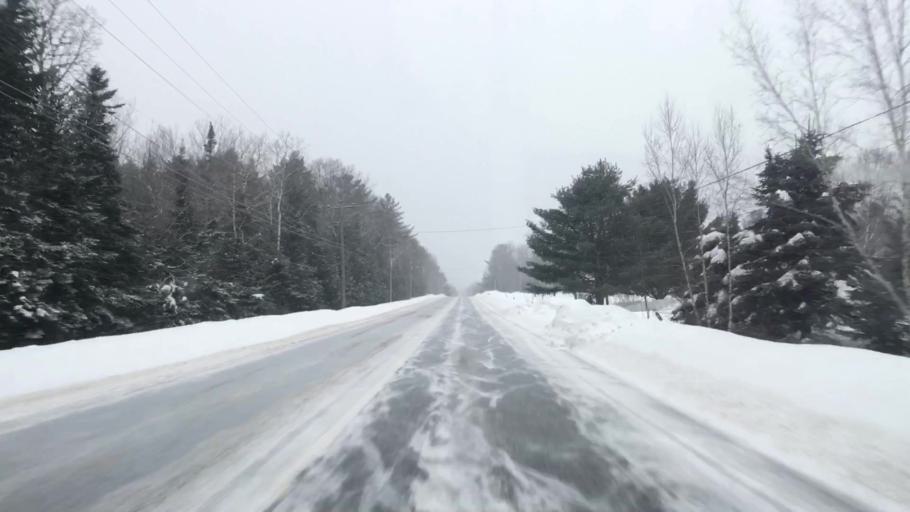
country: US
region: Maine
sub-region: Penobscot County
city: Medway
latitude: 45.5467
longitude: -68.3743
